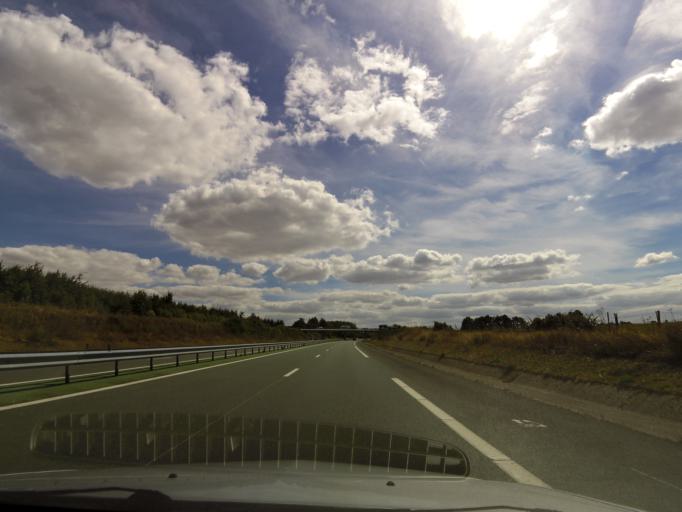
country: FR
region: Pays de la Loire
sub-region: Departement de la Vendee
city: Les Essarts
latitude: 46.7485
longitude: -1.2664
